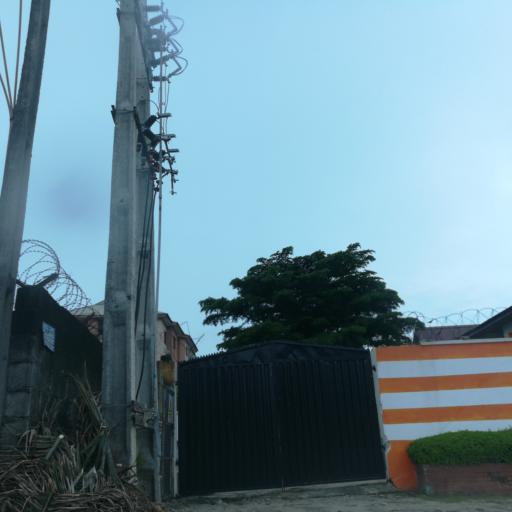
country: NG
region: Lagos
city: Ikoyi
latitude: 6.4431
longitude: 3.4690
